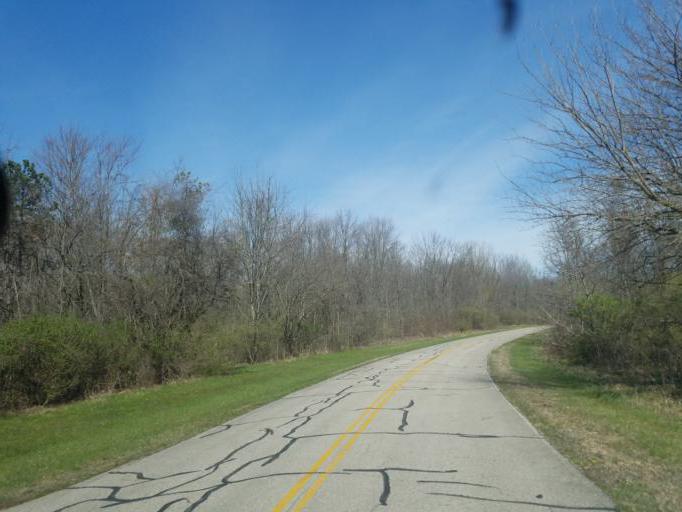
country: US
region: Ohio
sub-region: Delaware County
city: Delaware
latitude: 40.3720
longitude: -83.0682
